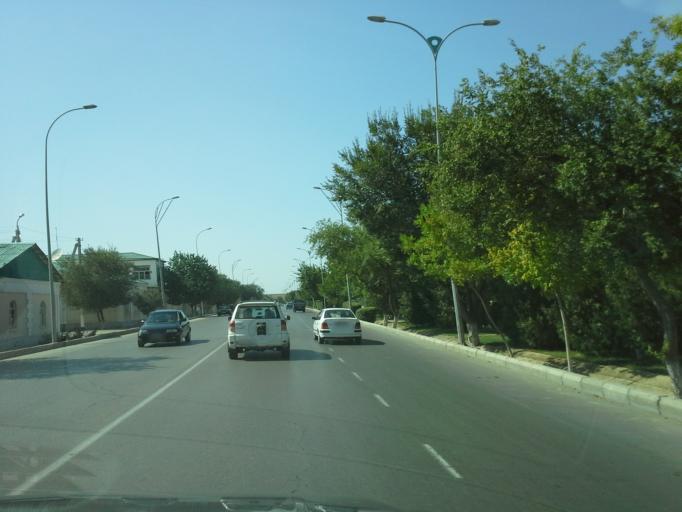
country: TM
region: Dasoguz
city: Dasoguz
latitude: 41.8393
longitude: 59.9478
